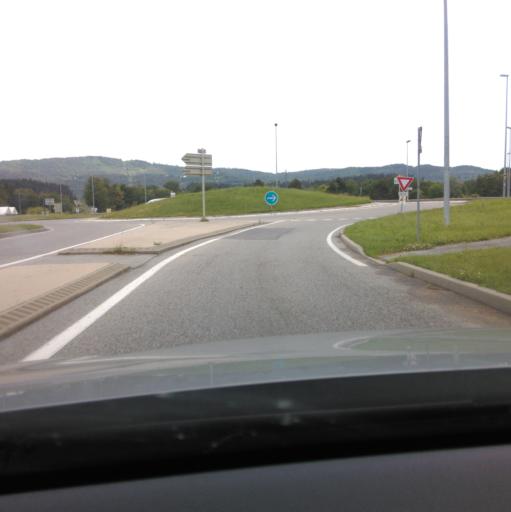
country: FR
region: Rhone-Alpes
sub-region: Departement de l'Ain
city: Montreal-la-Cluse
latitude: 46.1791
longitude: 5.5505
